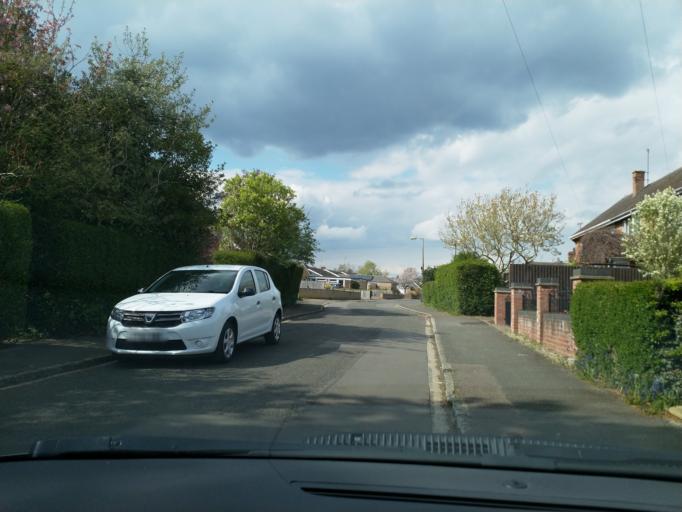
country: GB
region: England
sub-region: Oxfordshire
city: Adderbury
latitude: 52.0212
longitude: -1.3069
